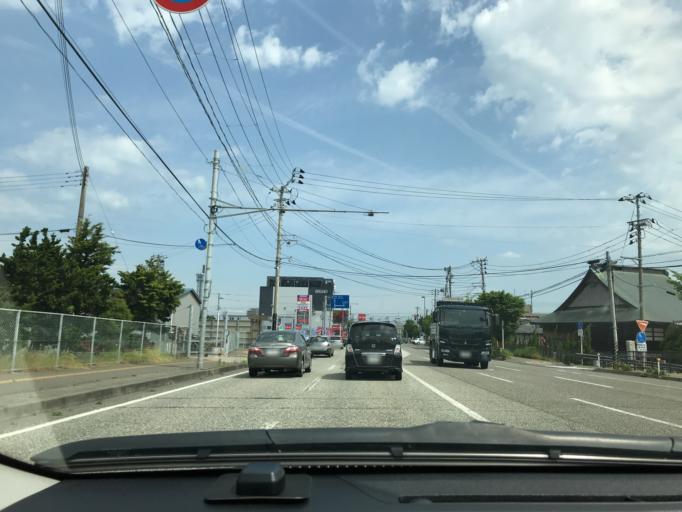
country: JP
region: Niigata
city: Niigata-shi
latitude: 37.8849
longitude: 139.0190
